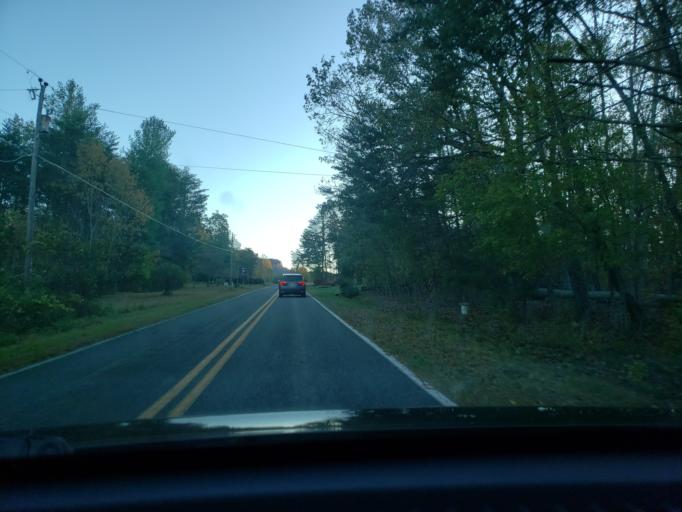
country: US
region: North Carolina
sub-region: Stokes County
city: Danbury
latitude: 36.4218
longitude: -80.2430
